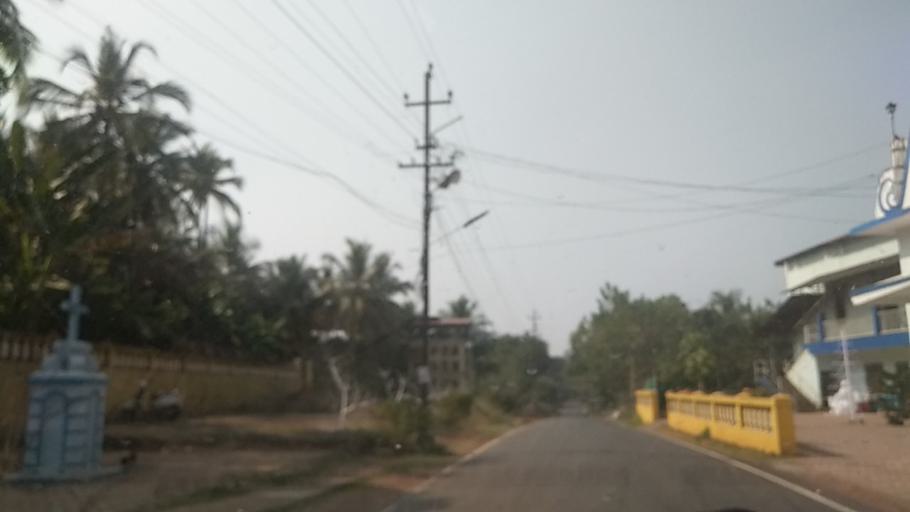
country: IN
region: Goa
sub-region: South Goa
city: Cortalim
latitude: 15.3950
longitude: 73.9268
